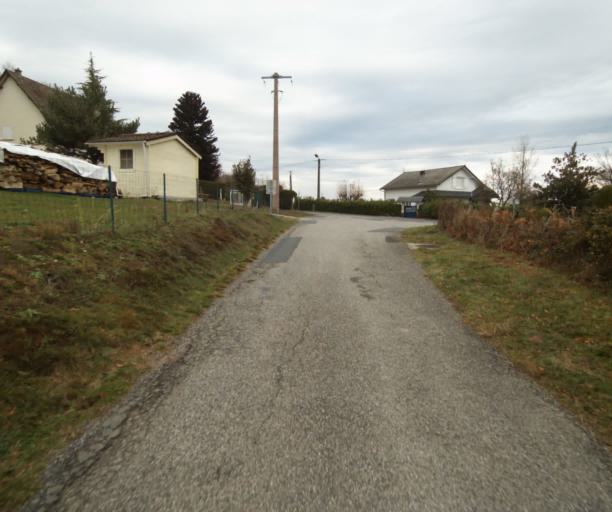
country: FR
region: Limousin
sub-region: Departement de la Correze
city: Sainte-Fortunade
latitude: 45.2259
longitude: 1.7651
